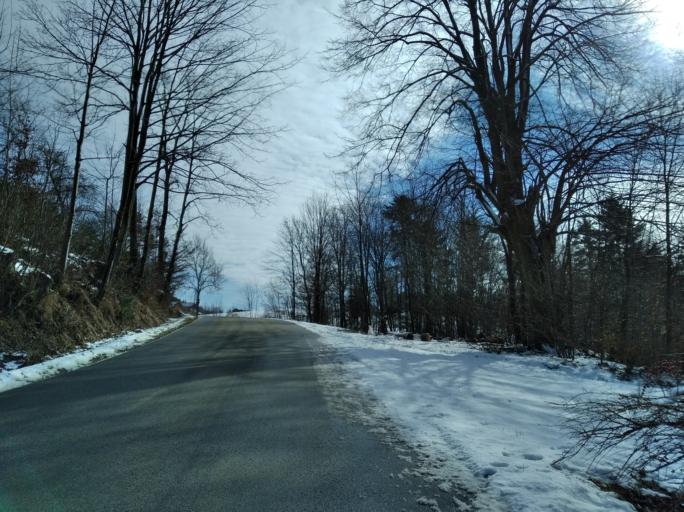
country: PL
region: Subcarpathian Voivodeship
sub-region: Powiat brzozowski
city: Jablonica Polska
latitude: 49.7295
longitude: 21.8977
